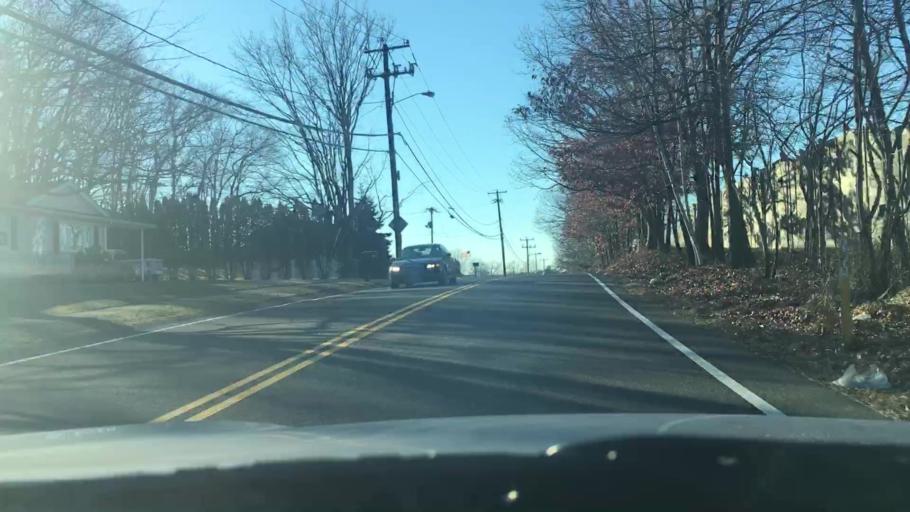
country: US
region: Massachusetts
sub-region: Hampden County
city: Ludlow
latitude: 42.1659
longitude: -72.4896
